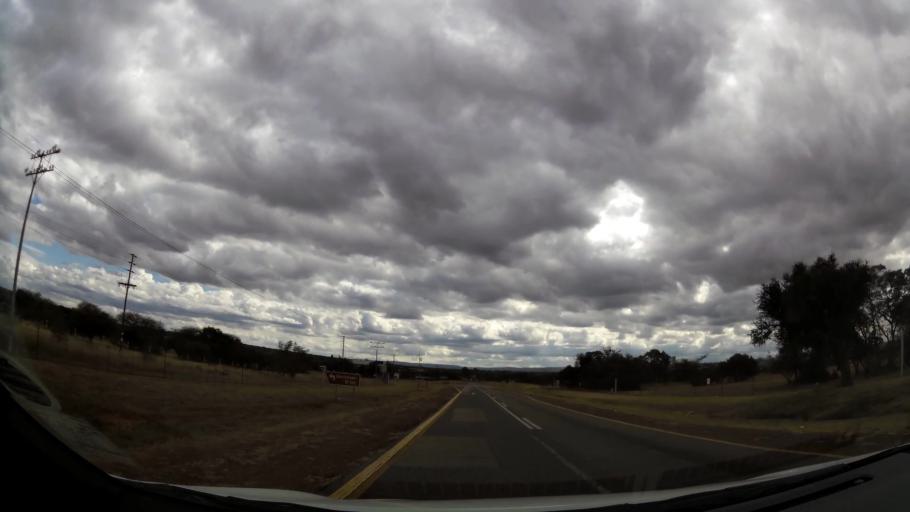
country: ZA
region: Limpopo
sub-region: Waterberg District Municipality
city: Modimolle
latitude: -24.7546
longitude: 28.4498
